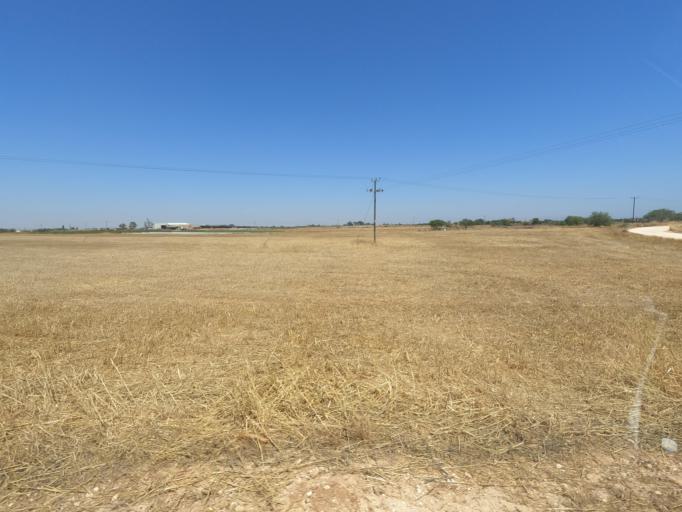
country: CY
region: Ammochostos
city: Liopetri
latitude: 35.0317
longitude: 33.8979
